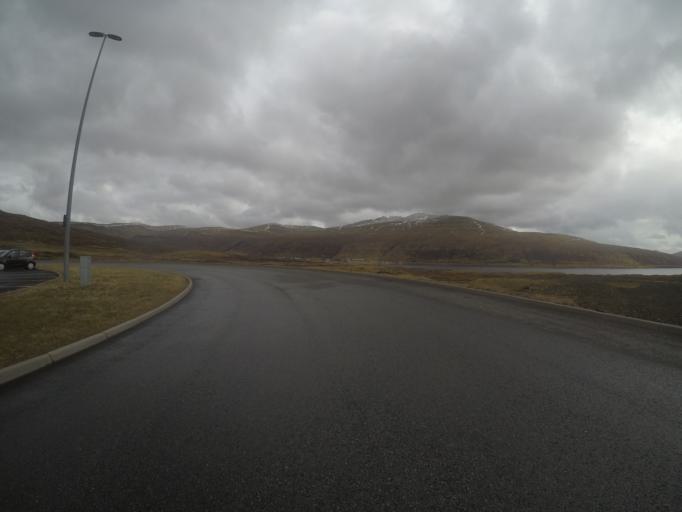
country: FO
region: Vagar
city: Midvagur
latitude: 62.0676
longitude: -7.2750
